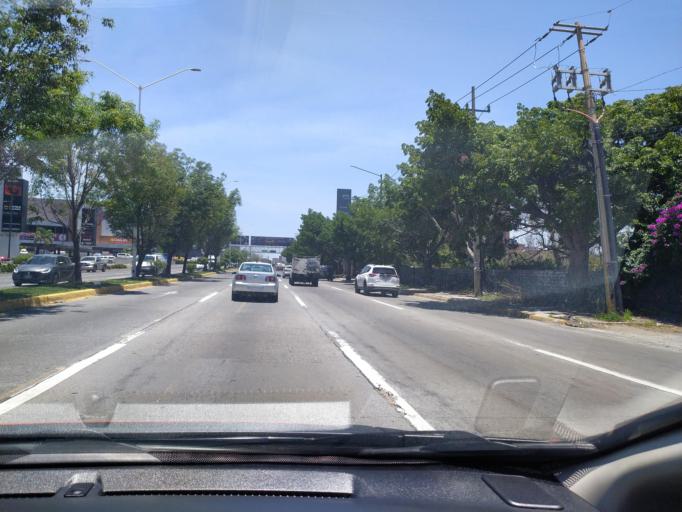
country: MX
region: Jalisco
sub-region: Tlajomulco de Zuniga
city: La Tijera
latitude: 20.5680
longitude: -103.4572
